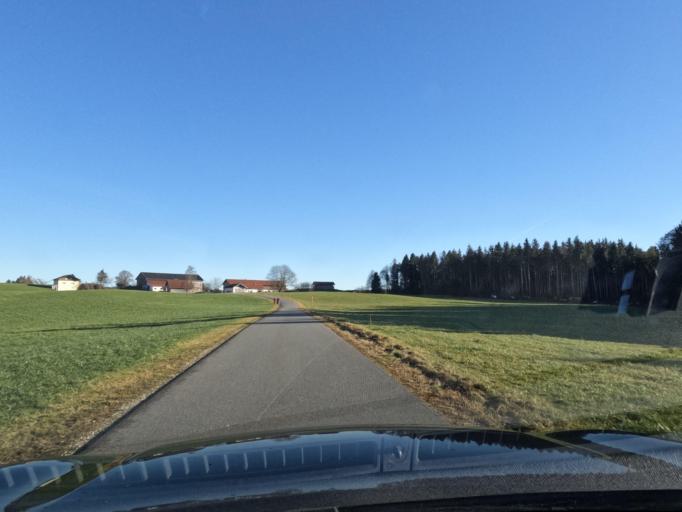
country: DE
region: Bavaria
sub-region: Upper Bavaria
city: Surberg
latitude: 47.8896
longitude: 12.6962
